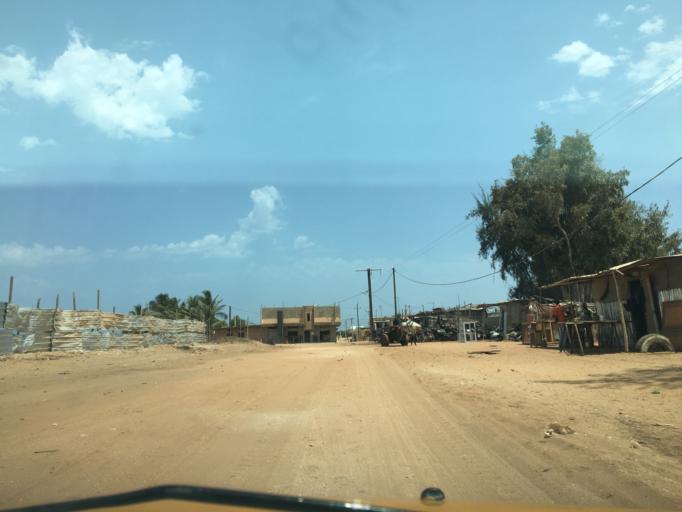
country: SN
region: Thies
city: Thies
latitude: 14.8062
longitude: -17.1874
